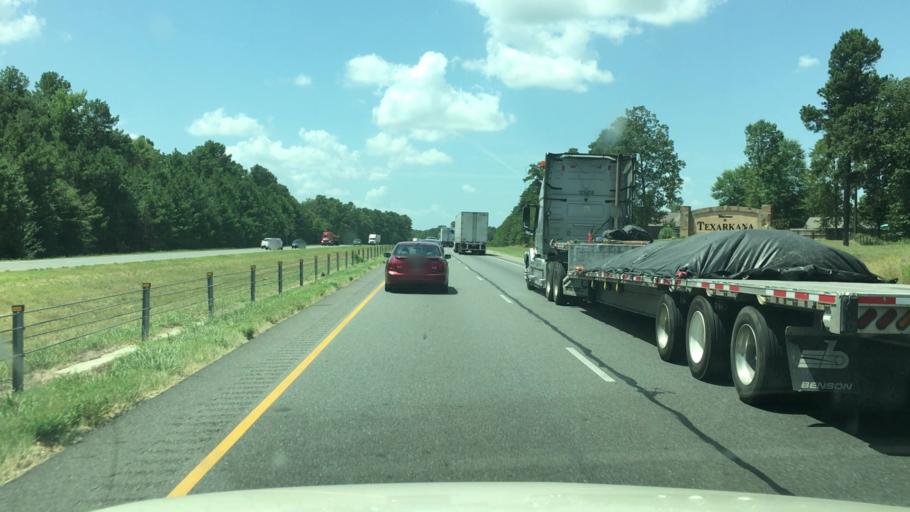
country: US
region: Arkansas
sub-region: Miller County
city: Texarkana
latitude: 33.4864
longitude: -93.9751
